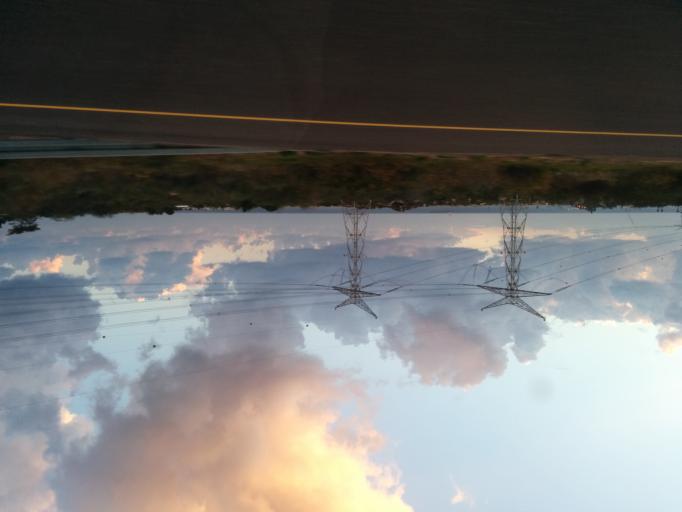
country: IL
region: Haifa
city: Hadera
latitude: 32.4747
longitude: 34.9024
